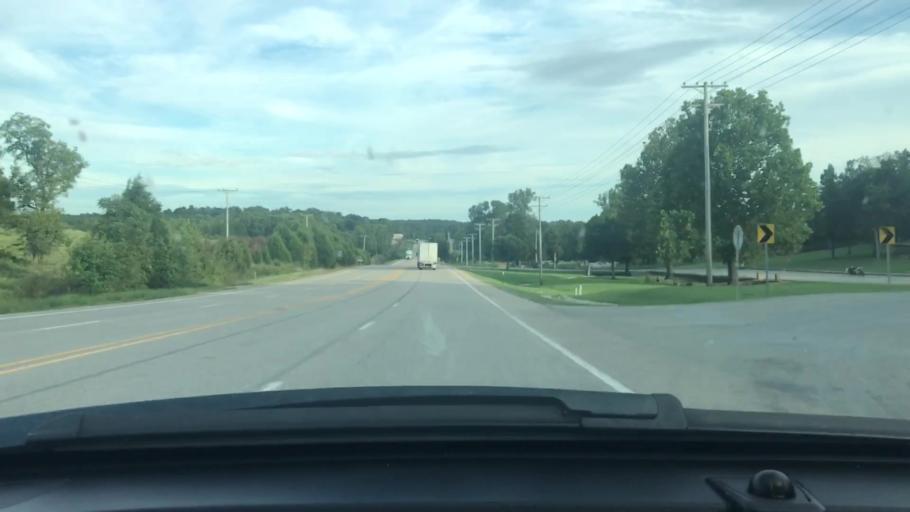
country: US
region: Arkansas
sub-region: Lawrence County
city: Hoxie
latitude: 36.1241
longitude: -91.1528
